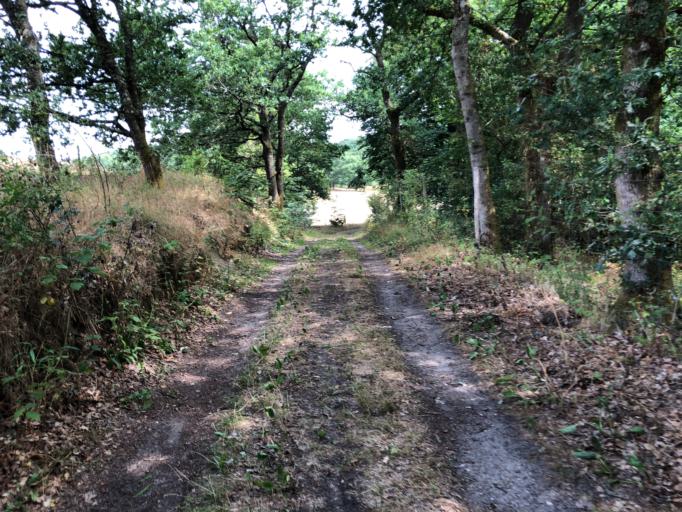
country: DK
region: South Denmark
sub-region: Vejle Kommune
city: Egtved
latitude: 55.6559
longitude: 9.2908
